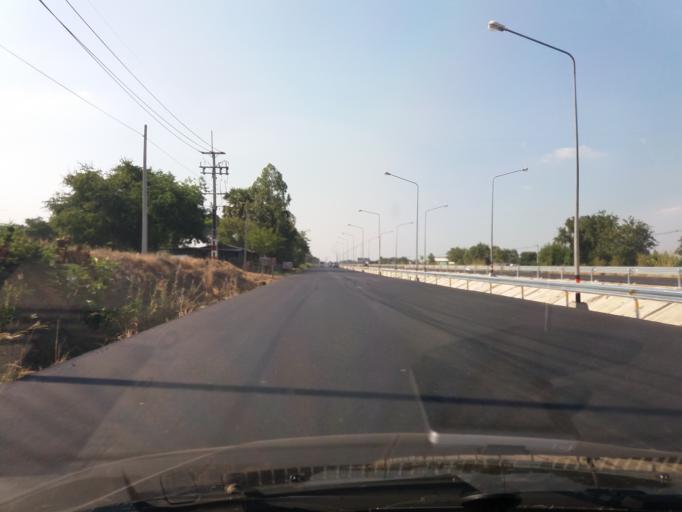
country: TH
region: Nakhon Sawan
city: Krok Phra
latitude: 15.6198
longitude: 100.1164
